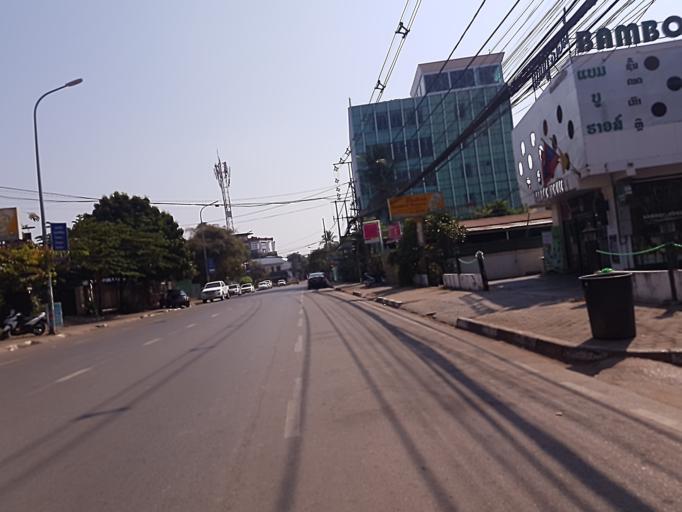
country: LA
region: Vientiane
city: Vientiane
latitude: 17.9742
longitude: 102.6307
